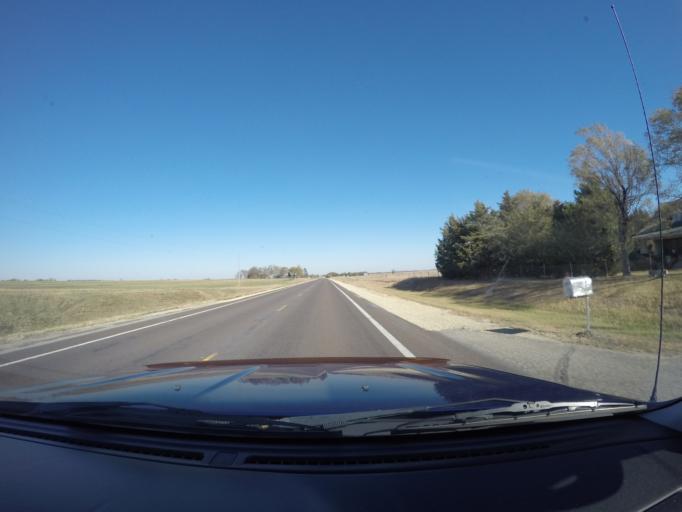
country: US
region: Kansas
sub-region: Marshall County
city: Blue Rapids
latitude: 39.6031
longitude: -96.7501
